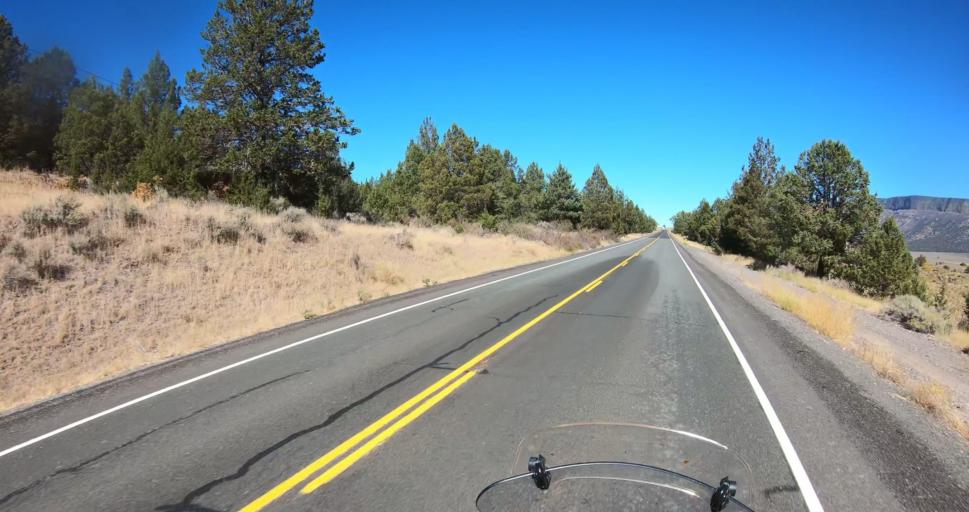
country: US
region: Oregon
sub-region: Lake County
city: Lakeview
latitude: 42.4314
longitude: -120.2821
